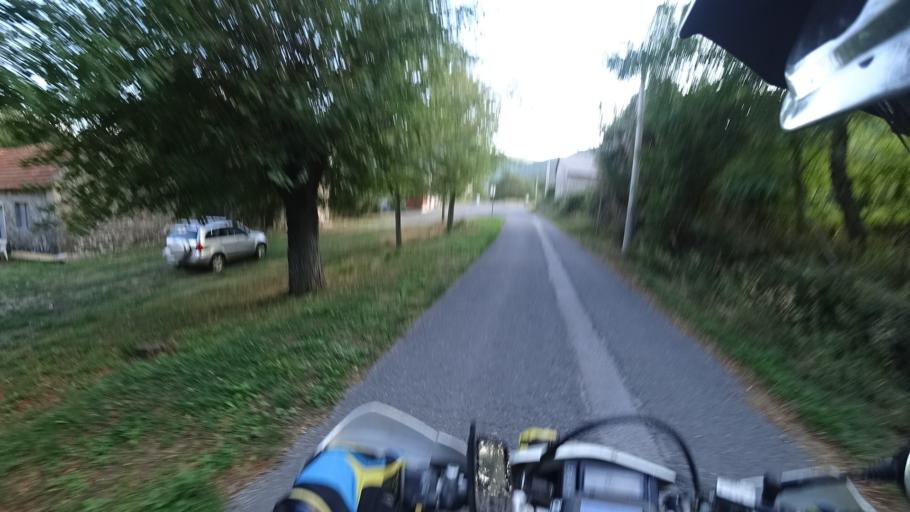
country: HR
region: Sibensko-Kniniska
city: Knin
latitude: 44.1945
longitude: 16.0557
